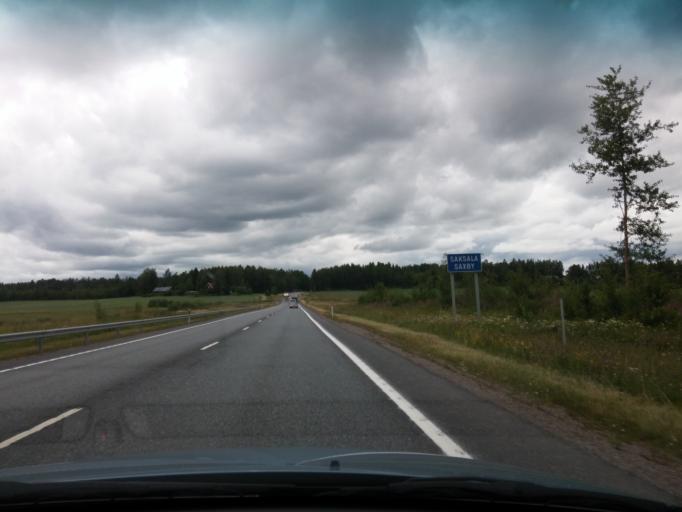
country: FI
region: Uusimaa
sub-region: Porvoo
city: Porvoo
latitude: 60.4134
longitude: 25.5815
